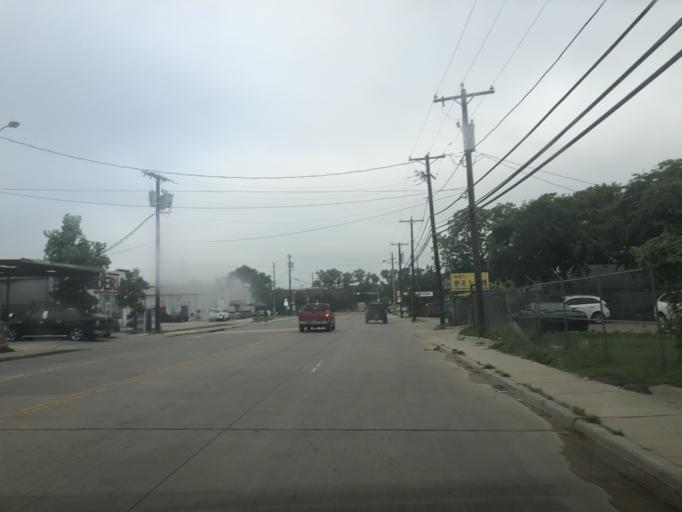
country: US
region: Texas
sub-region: Dallas County
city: Farmers Branch
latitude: 32.8677
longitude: -96.8755
